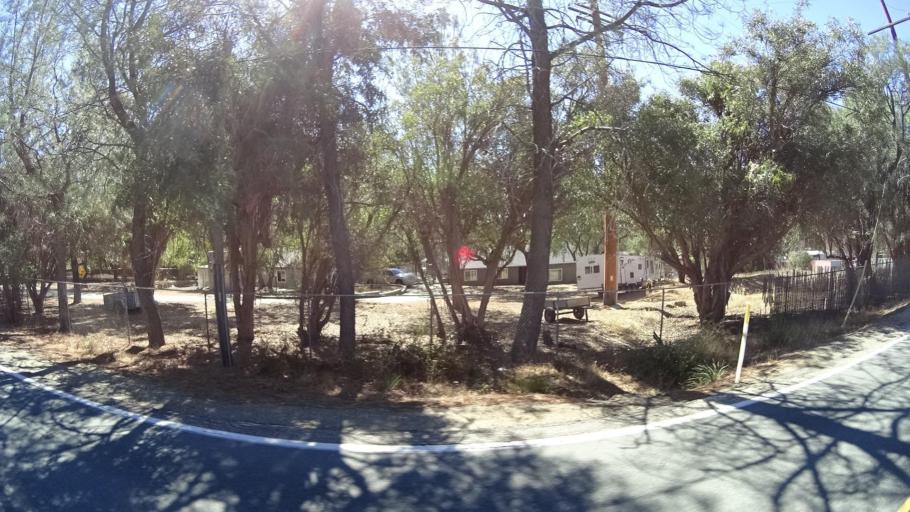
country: US
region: California
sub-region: San Diego County
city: Descanso
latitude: 32.8018
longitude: -116.6451
